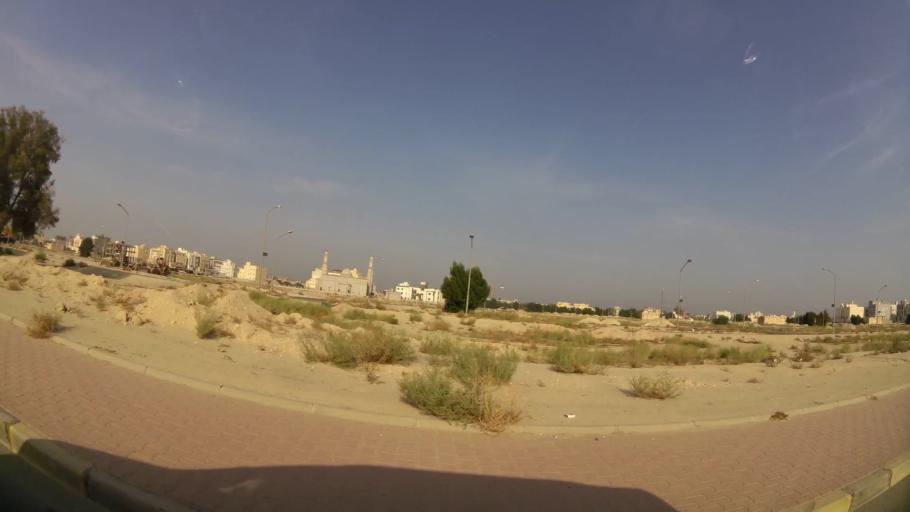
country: KW
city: Al Funaytis
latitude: 29.2068
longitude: 48.0996
